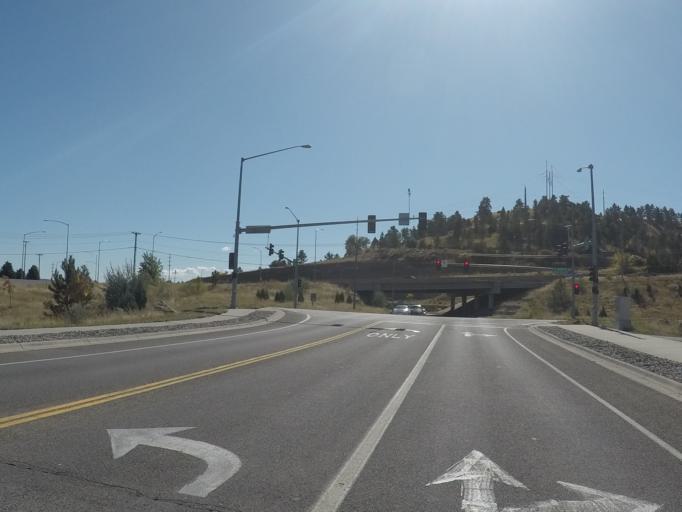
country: US
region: Montana
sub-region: Yellowstone County
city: Billings
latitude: 45.8045
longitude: -108.4842
